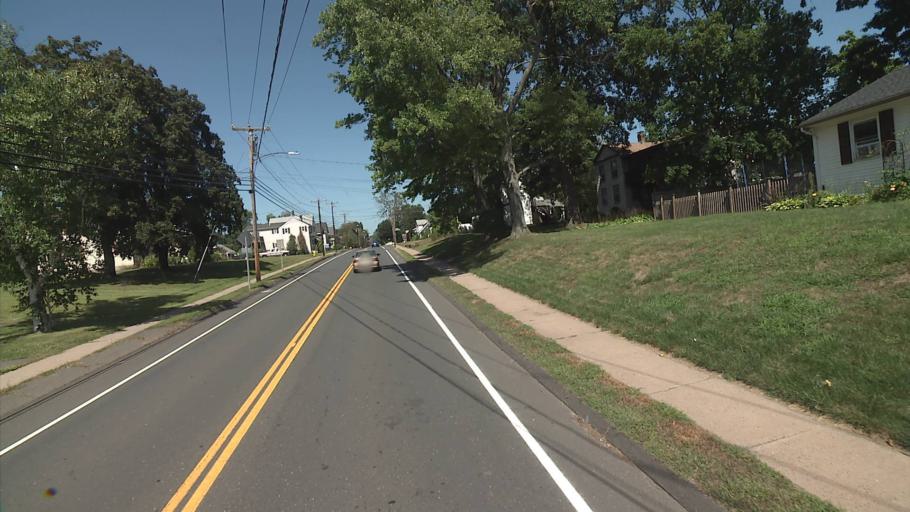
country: US
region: Connecticut
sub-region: Hartford County
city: Windsor Locks
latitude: 41.9389
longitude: -72.6296
